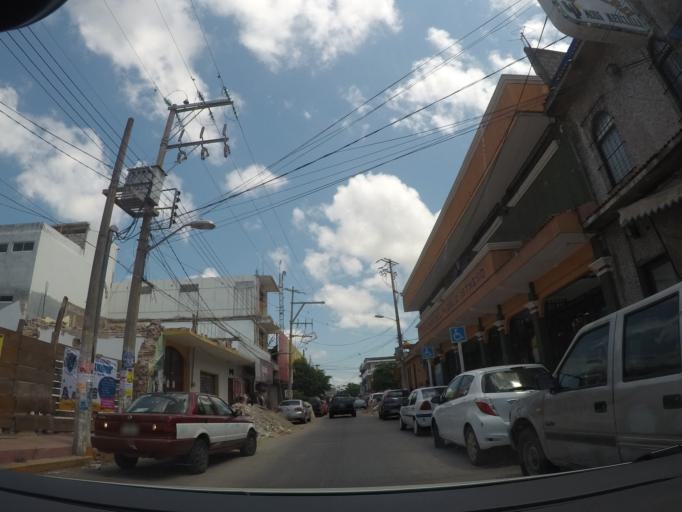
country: MX
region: Oaxaca
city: Juchitan de Zaragoza
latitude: 16.4346
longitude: -95.0225
